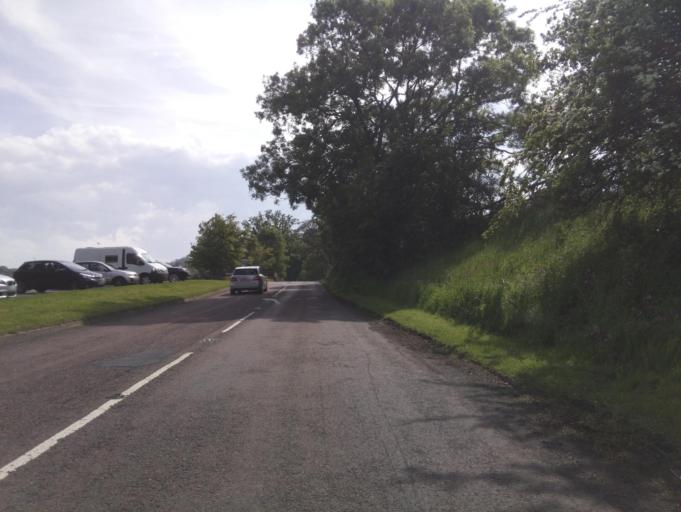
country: GB
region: England
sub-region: Northumberland
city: Alnwick
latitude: 55.4212
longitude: -1.7062
